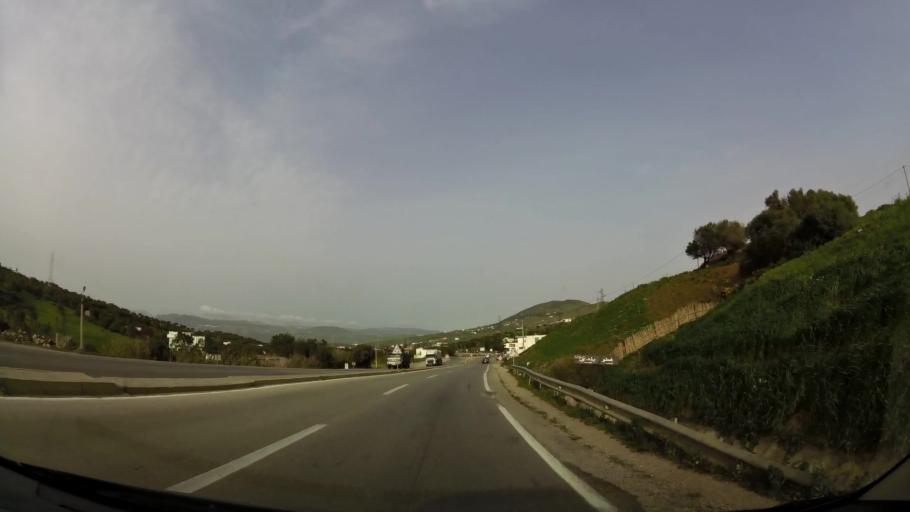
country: MA
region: Tanger-Tetouan
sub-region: Tetouan
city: Saddina
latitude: 35.5493
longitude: -5.5243
